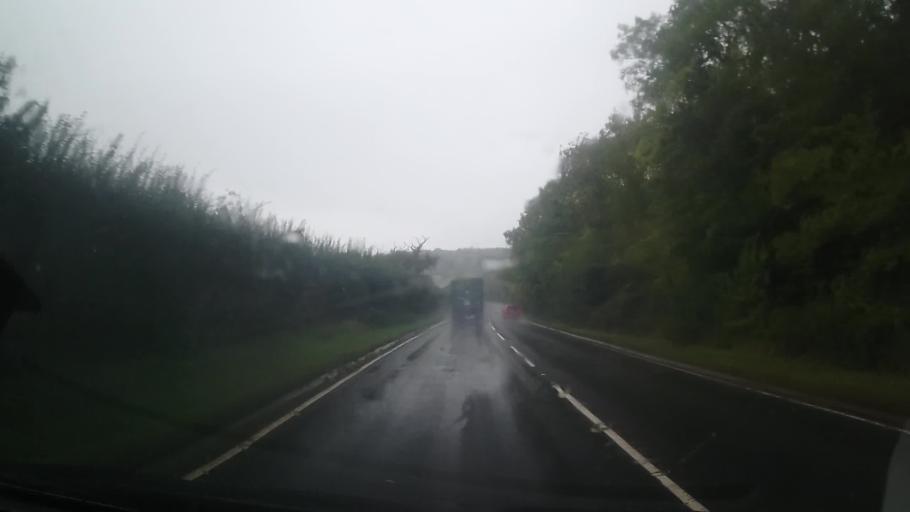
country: GB
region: England
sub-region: Worcestershire
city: Evesham
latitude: 52.1221
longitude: -1.9790
